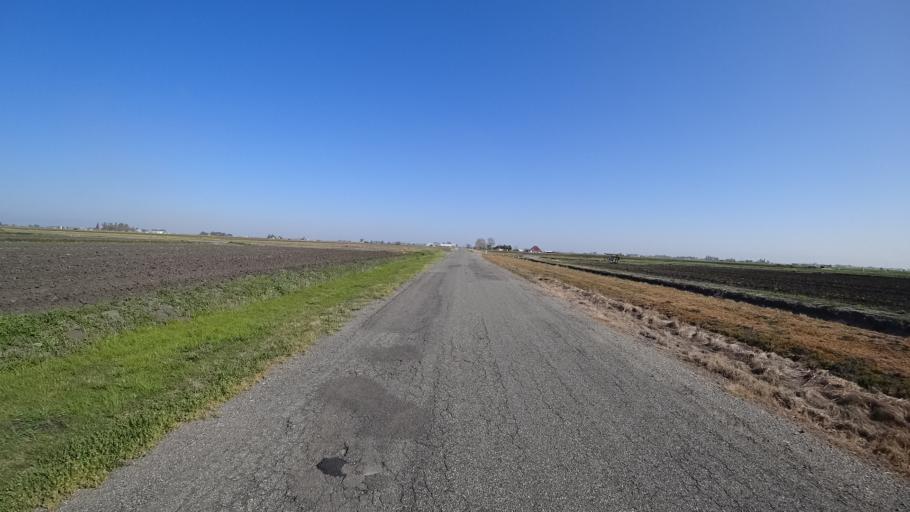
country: US
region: California
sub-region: Glenn County
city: Willows
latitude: 39.5642
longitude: -122.0839
